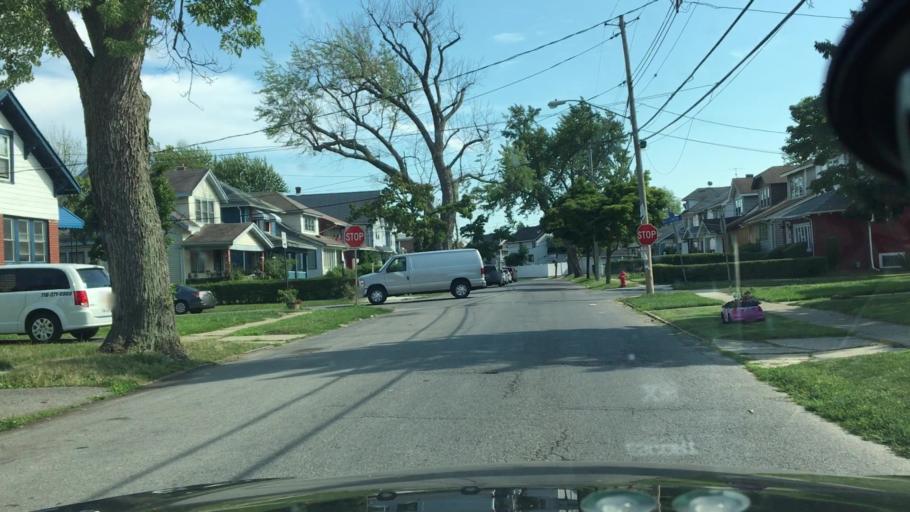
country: US
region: New York
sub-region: Erie County
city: Eggertsville
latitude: 42.9380
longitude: -78.8173
